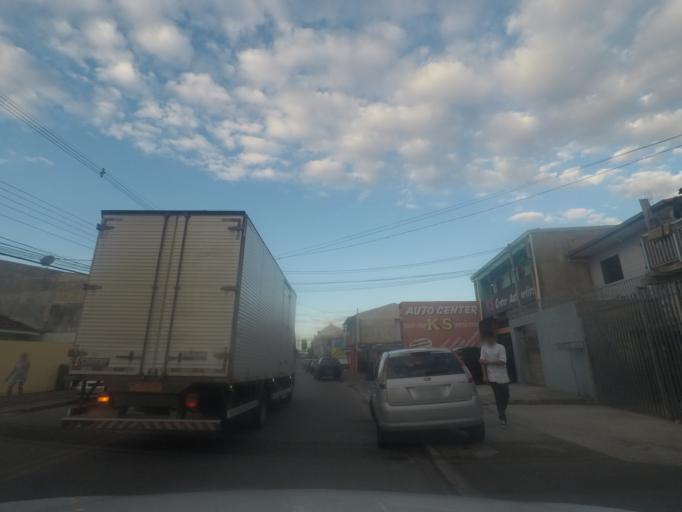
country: BR
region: Parana
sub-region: Pinhais
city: Pinhais
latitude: -25.4657
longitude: -49.1994
